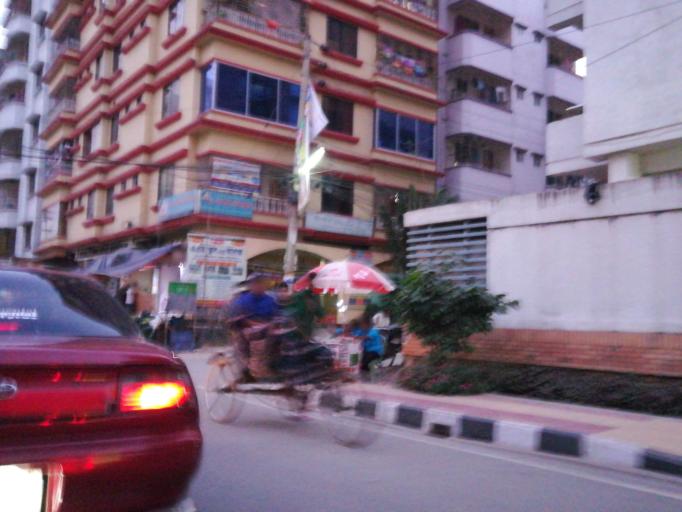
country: BD
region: Dhaka
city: Tungi
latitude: 23.8678
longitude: 90.3886
